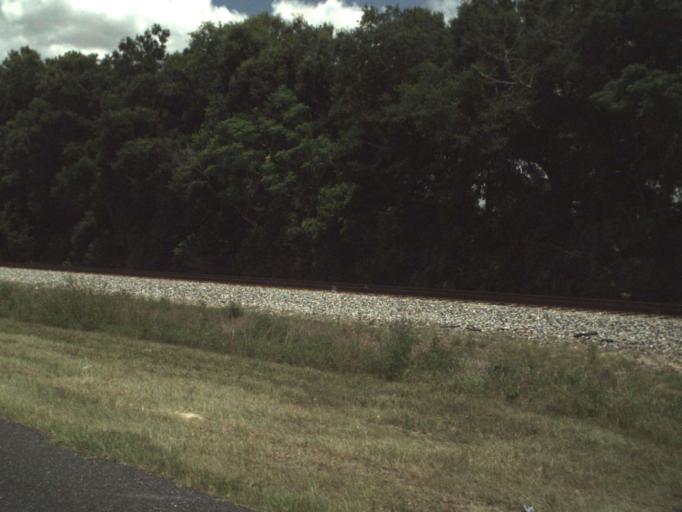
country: US
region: Florida
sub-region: Sumter County
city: The Villages
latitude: 28.9604
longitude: -82.0405
